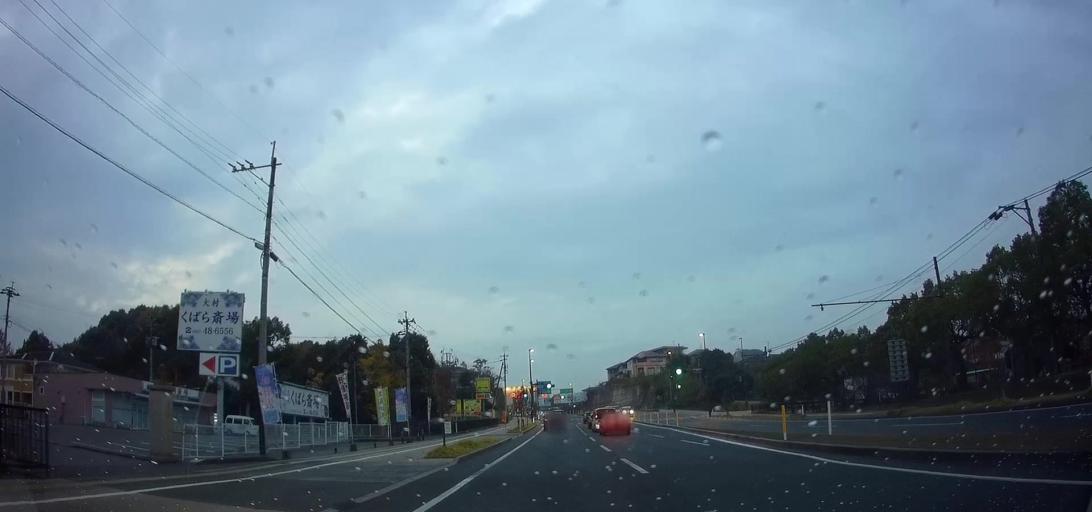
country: JP
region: Nagasaki
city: Omura
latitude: 32.8924
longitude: 129.9693
